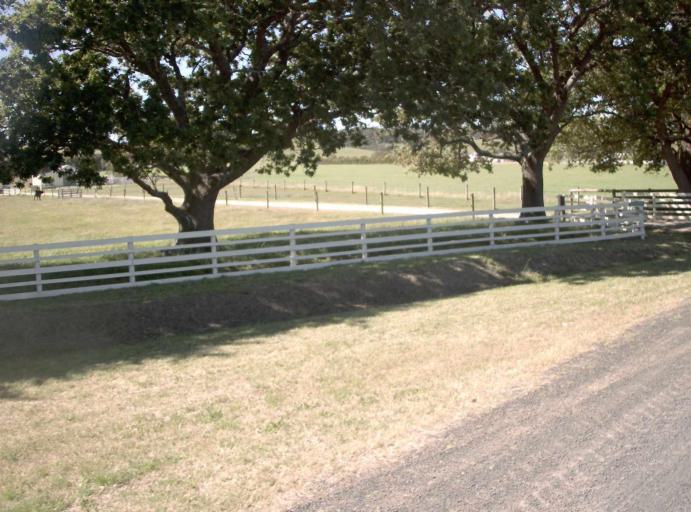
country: AU
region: Victoria
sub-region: Latrobe
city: Morwell
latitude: -38.6585
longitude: 146.4550
